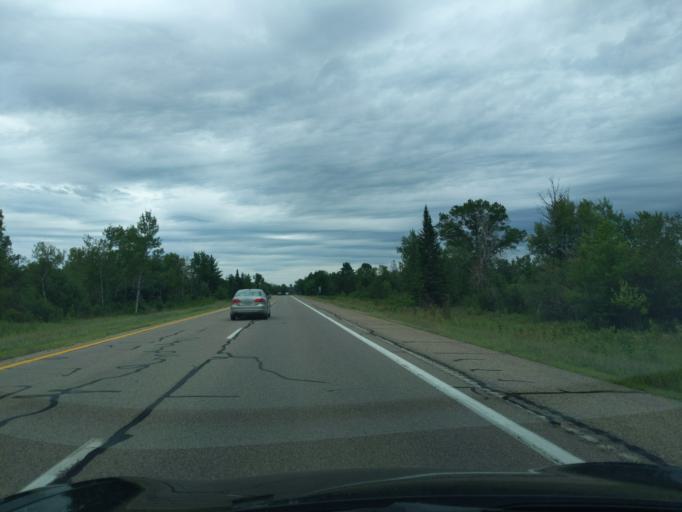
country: US
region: Michigan
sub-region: Roscommon County
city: Houghton Lake
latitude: 44.3044
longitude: -84.8039
